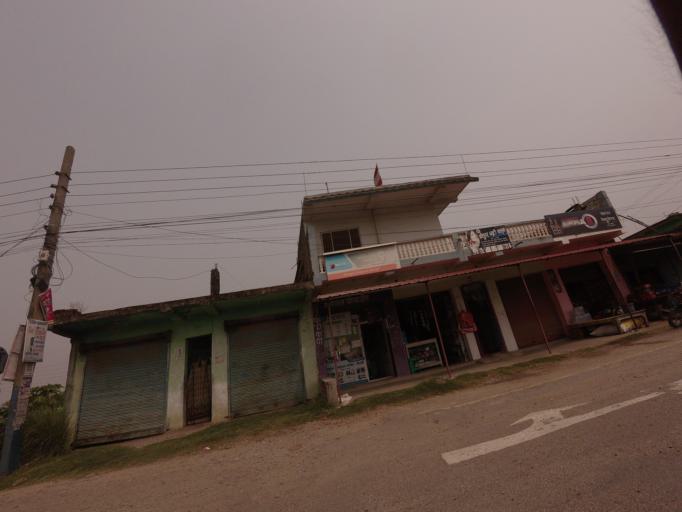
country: NP
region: Western Region
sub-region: Lumbini Zone
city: Bhairahawa
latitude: 27.5136
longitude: 83.3911
